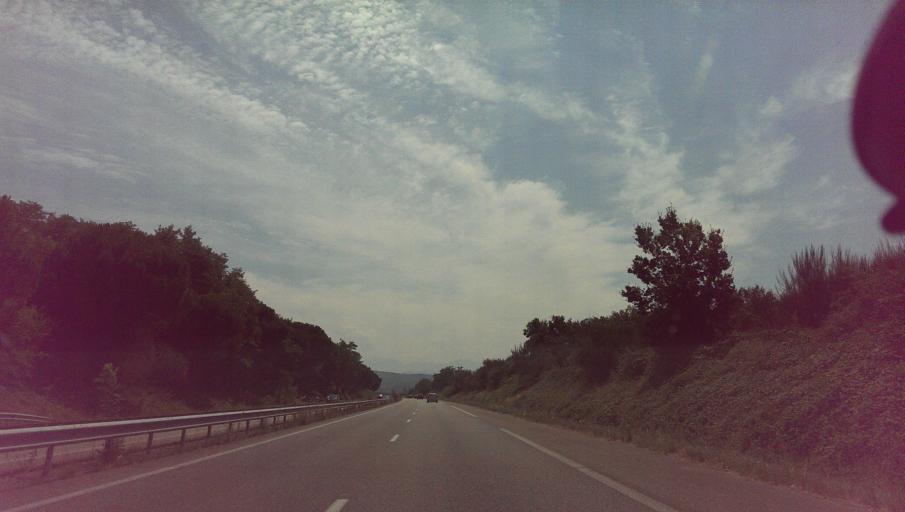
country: FR
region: Midi-Pyrenees
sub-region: Departement de l'Ariege
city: Verniolle
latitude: 43.0774
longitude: 1.6384
